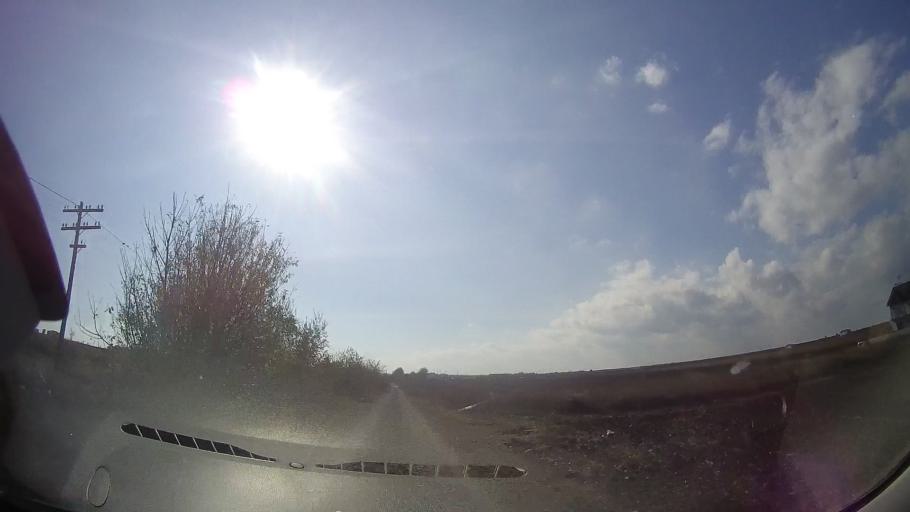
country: RO
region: Constanta
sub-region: Comuna Costinesti
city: Costinesti
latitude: 43.9668
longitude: 28.6406
